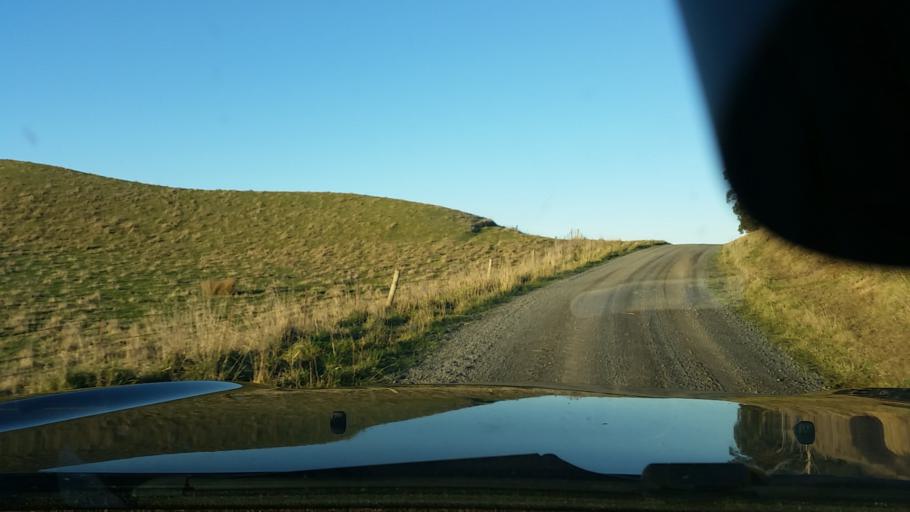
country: NZ
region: Marlborough
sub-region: Marlborough District
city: Blenheim
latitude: -41.7494
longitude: 174.0691
